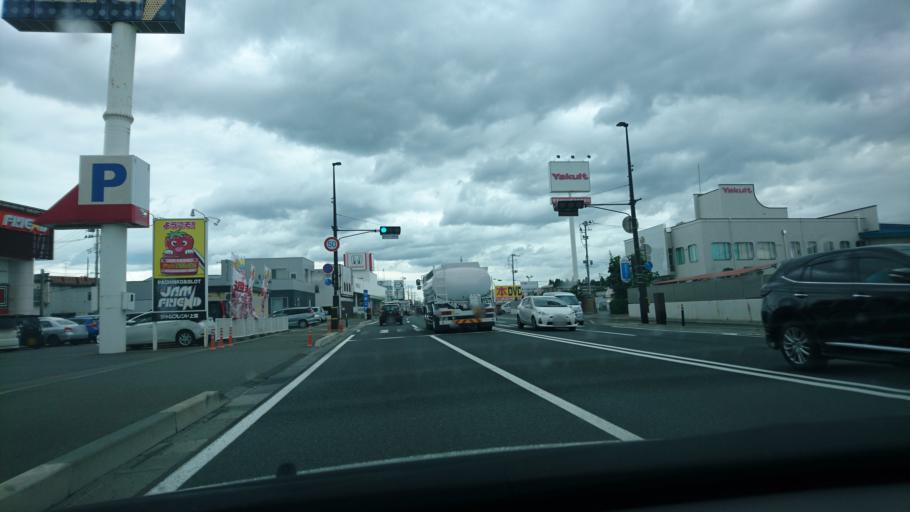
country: JP
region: Iwate
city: Morioka-shi
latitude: 39.7318
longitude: 141.1231
